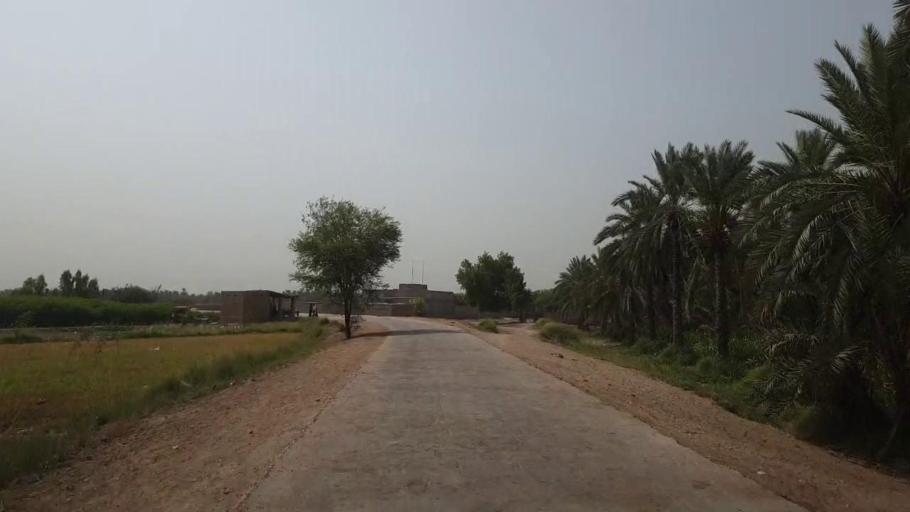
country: PK
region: Sindh
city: Gambat
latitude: 27.4275
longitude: 68.5370
